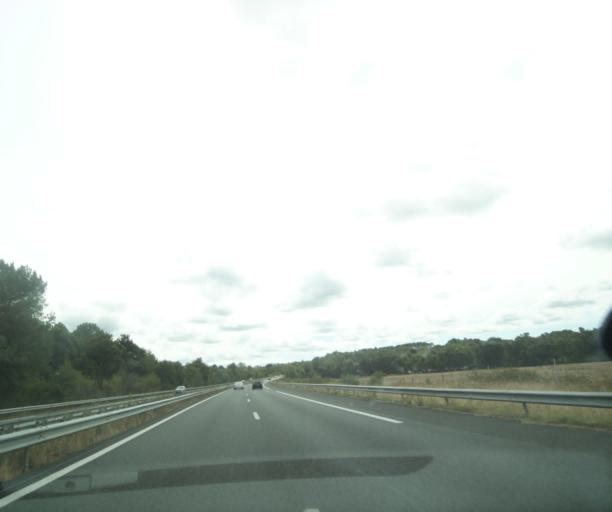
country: FR
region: Aquitaine
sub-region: Departement de la Gironde
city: Reignac
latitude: 45.2240
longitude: -0.5136
